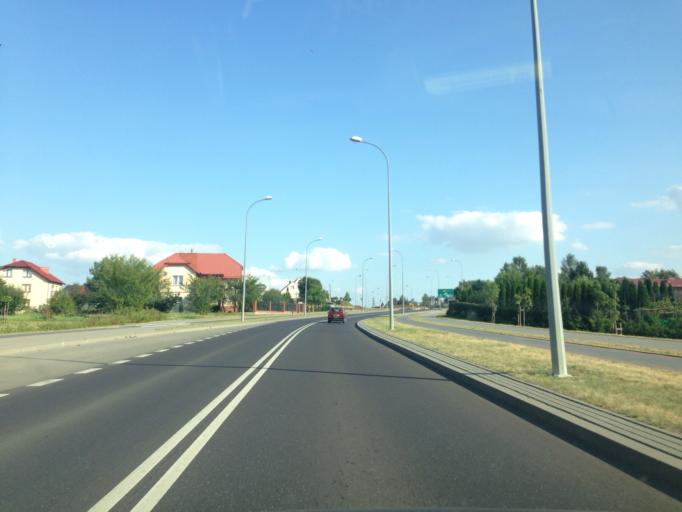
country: PL
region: Warmian-Masurian Voivodeship
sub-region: Powiat ilawski
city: Ilawa
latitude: 53.5979
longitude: 19.5755
